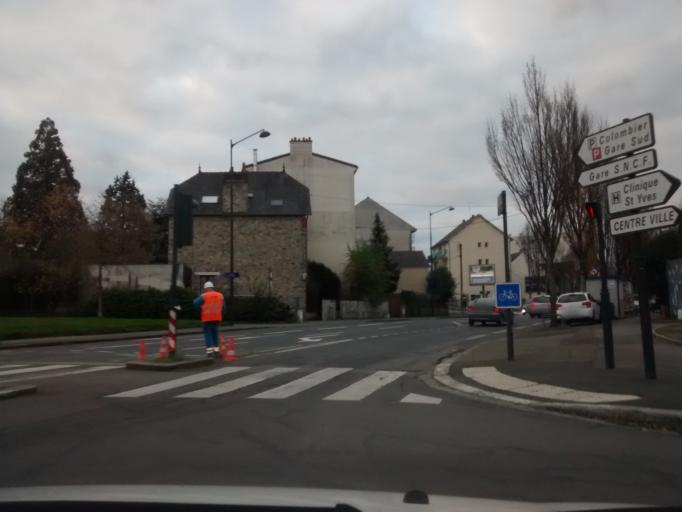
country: FR
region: Brittany
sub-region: Departement d'Ille-et-Vilaine
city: Rennes
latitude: 48.1004
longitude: -1.6500
